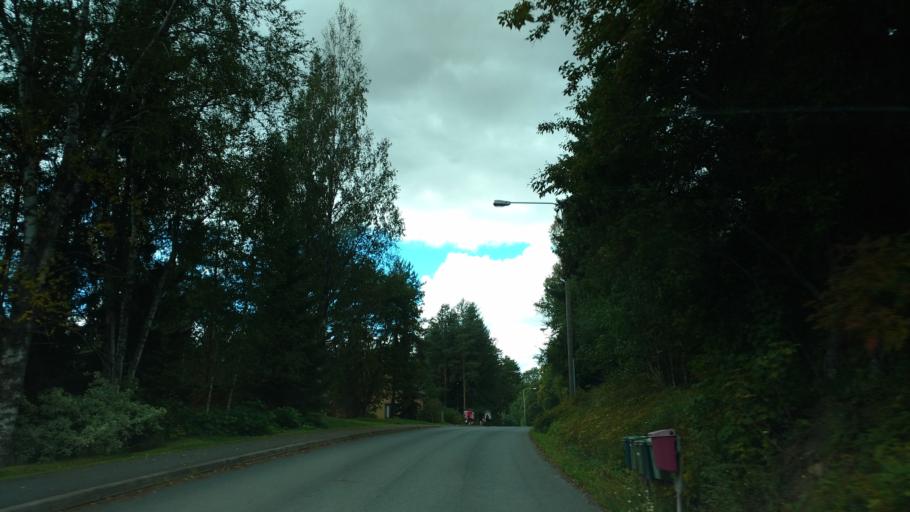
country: FI
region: Haeme
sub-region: Forssa
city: Ypaejae
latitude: 60.8062
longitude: 23.2696
